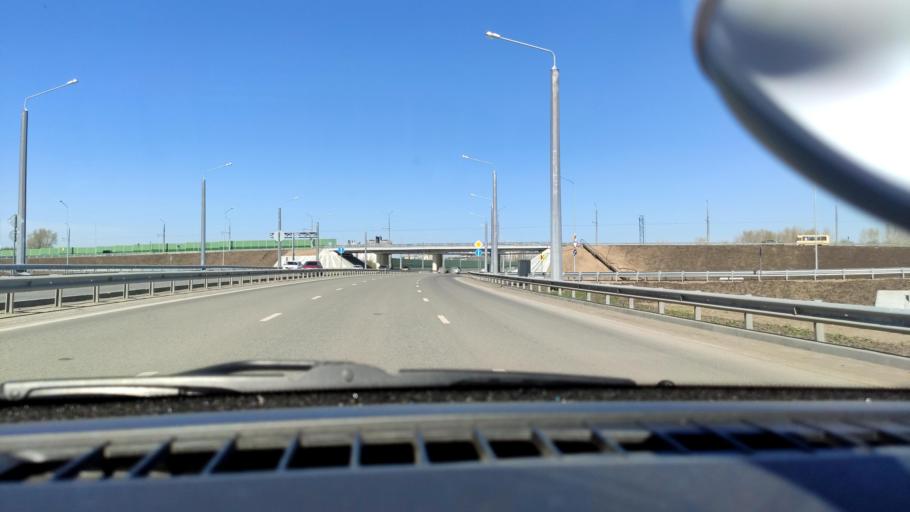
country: RU
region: Samara
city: Samara
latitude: 53.1639
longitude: 50.0878
